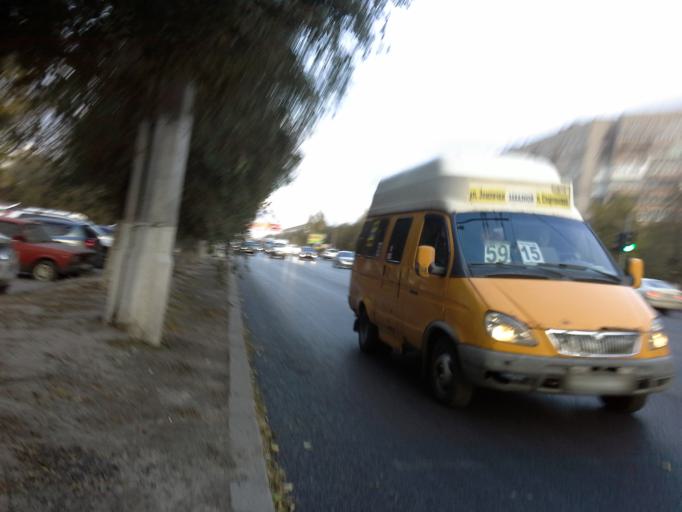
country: RU
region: Volgograd
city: Vodstroy
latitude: 48.8183
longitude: 44.6297
